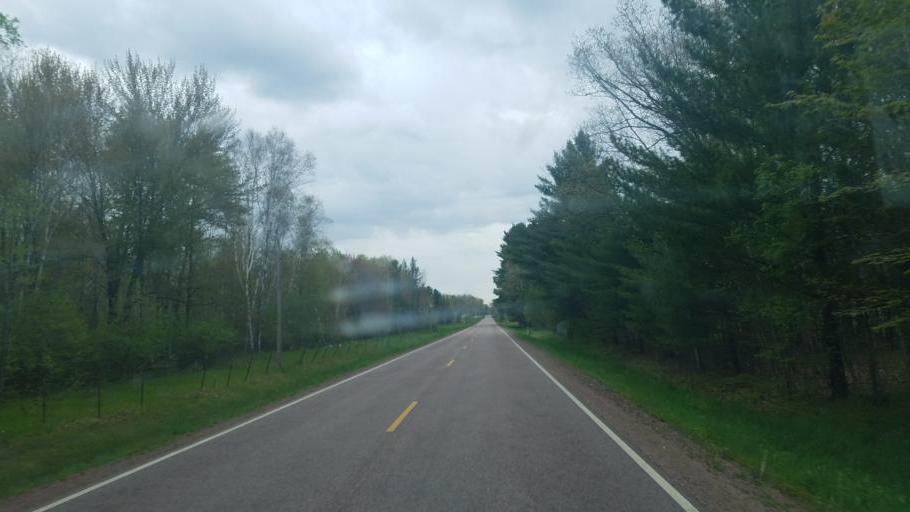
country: US
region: Wisconsin
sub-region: Wood County
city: Marshfield
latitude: 44.4605
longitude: -90.2800
